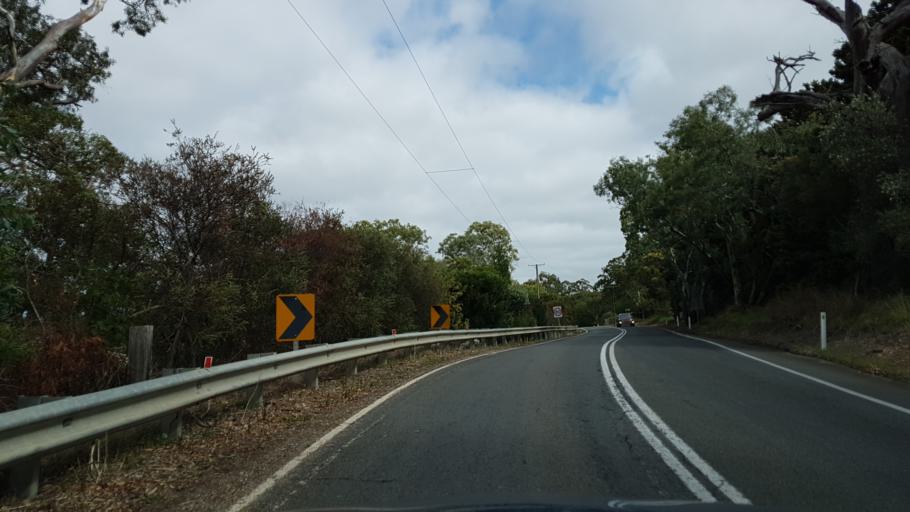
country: AU
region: South Australia
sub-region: Mount Barker
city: Nairne
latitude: -35.0416
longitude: 138.9270
